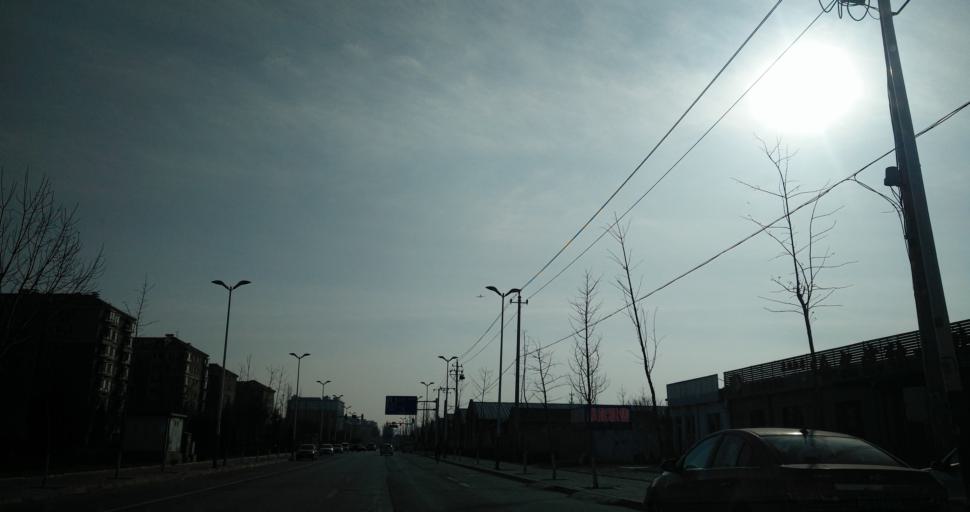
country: CN
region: Beijing
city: Xingfeng
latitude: 39.7141
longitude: 116.3912
